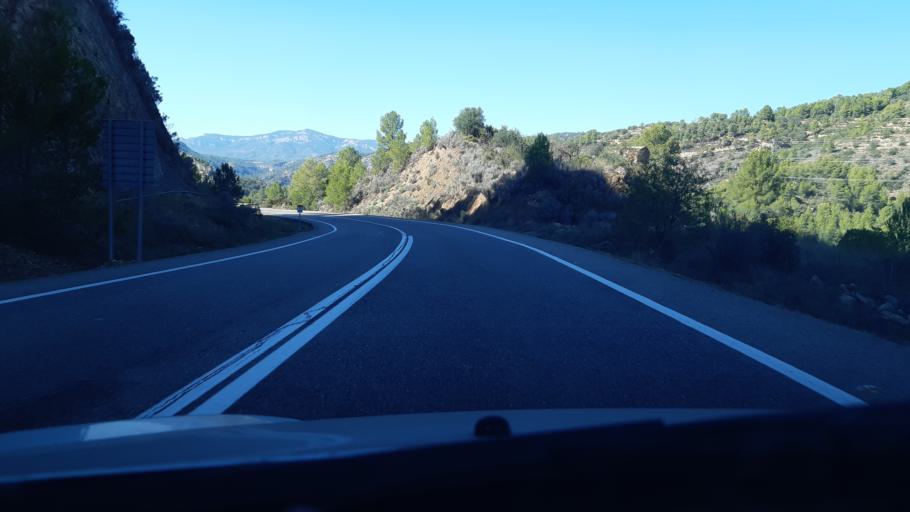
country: ES
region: Catalonia
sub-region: Provincia de Tarragona
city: Rasquera
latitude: 40.9953
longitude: 0.5676
